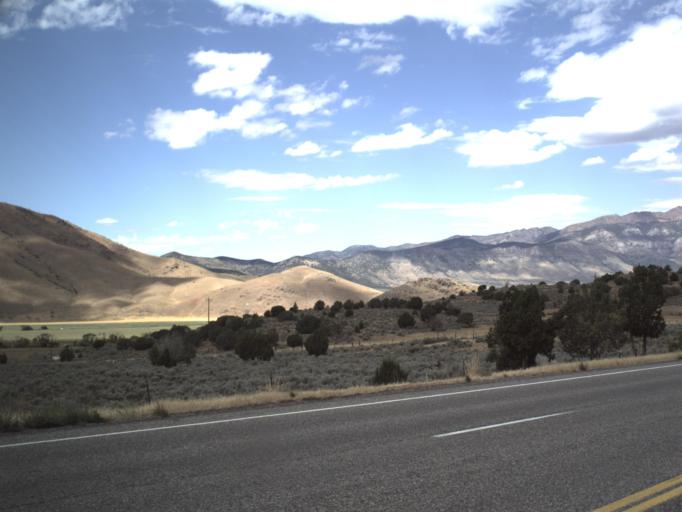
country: US
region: Utah
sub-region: Sanpete County
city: Gunnison
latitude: 39.2015
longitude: -112.0860
